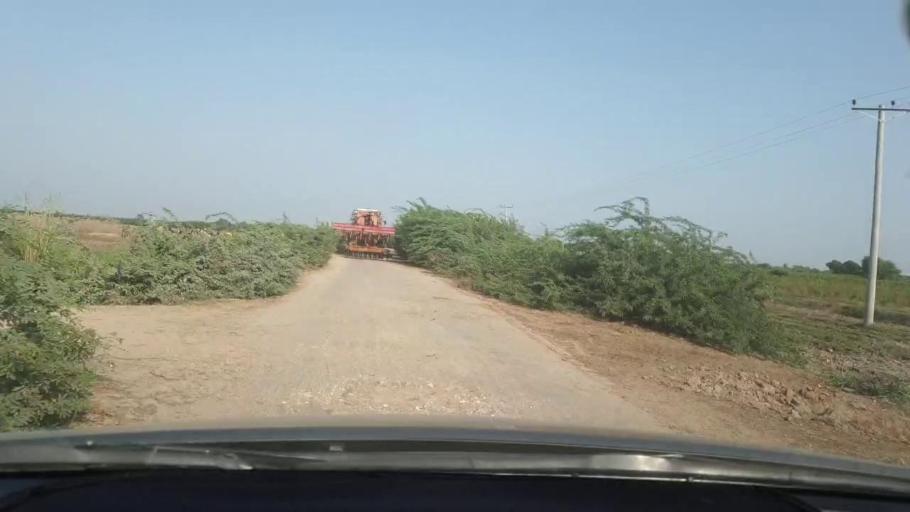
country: PK
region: Sindh
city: Naukot
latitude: 24.7666
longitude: 69.2407
